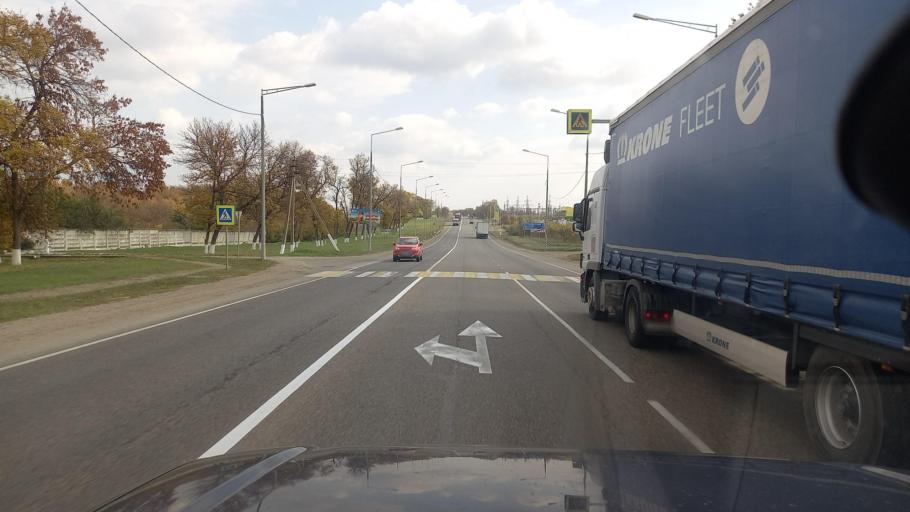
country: RU
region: Krasnodarskiy
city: Kholmskiy
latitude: 44.8480
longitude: 38.4142
